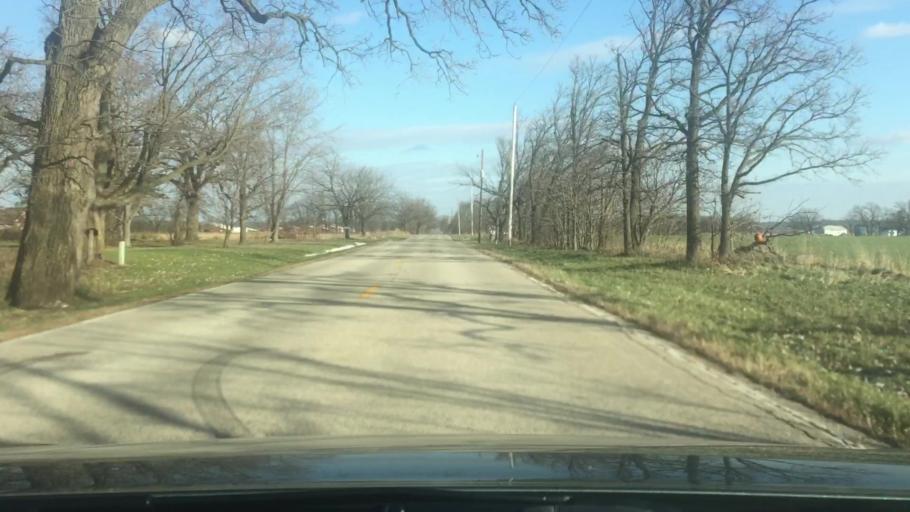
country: US
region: Wisconsin
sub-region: Jefferson County
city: Palmyra
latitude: 42.9173
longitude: -88.5319
